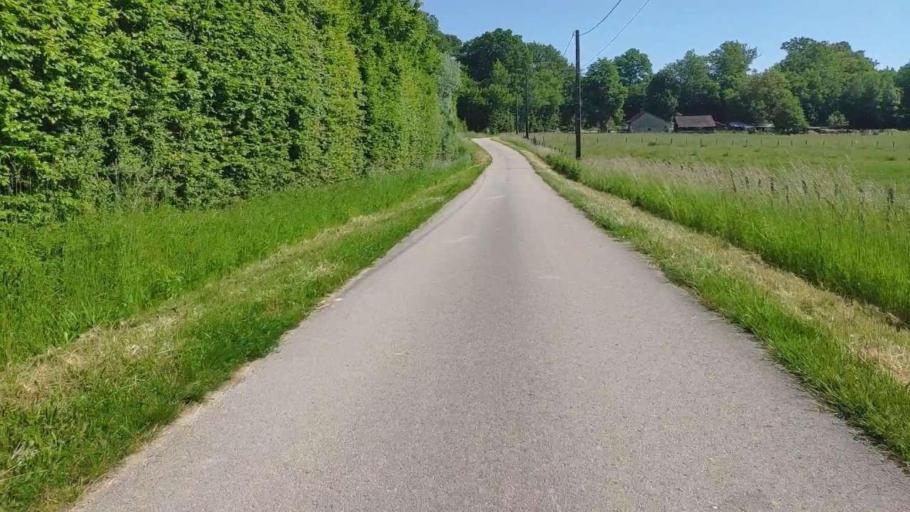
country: FR
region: Franche-Comte
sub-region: Departement du Jura
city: Bletterans
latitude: 46.7944
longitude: 5.4320
